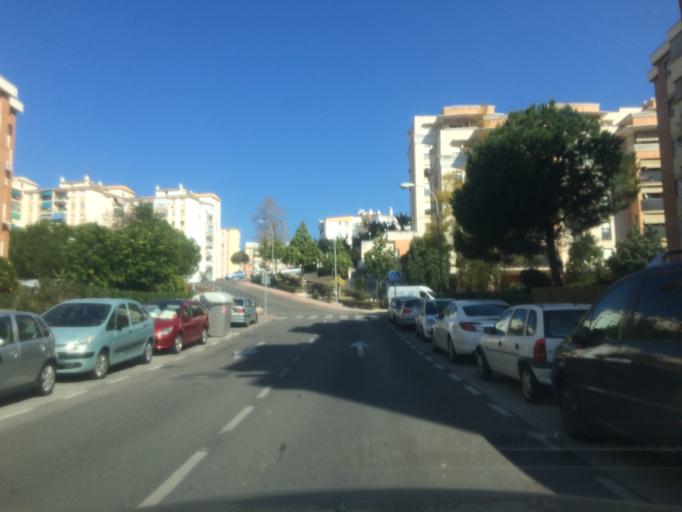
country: ES
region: Andalusia
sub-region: Provincia de Malaga
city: Malaga
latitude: 36.7479
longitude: -4.4172
